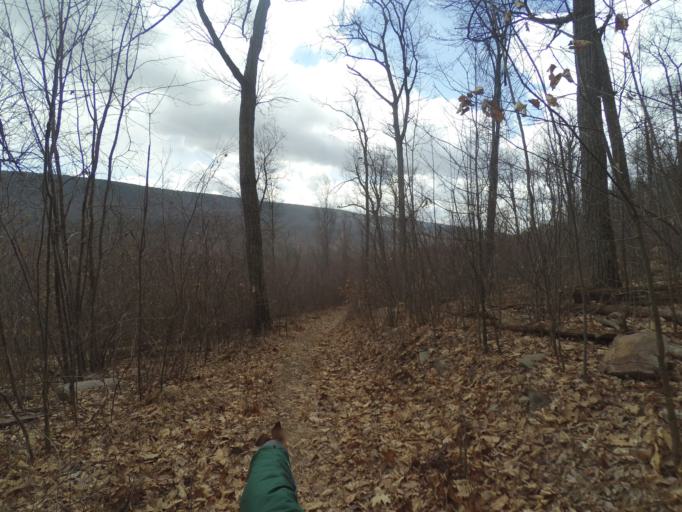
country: US
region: Pennsylvania
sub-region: Centre County
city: Boalsburg
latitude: 40.7604
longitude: -77.7155
